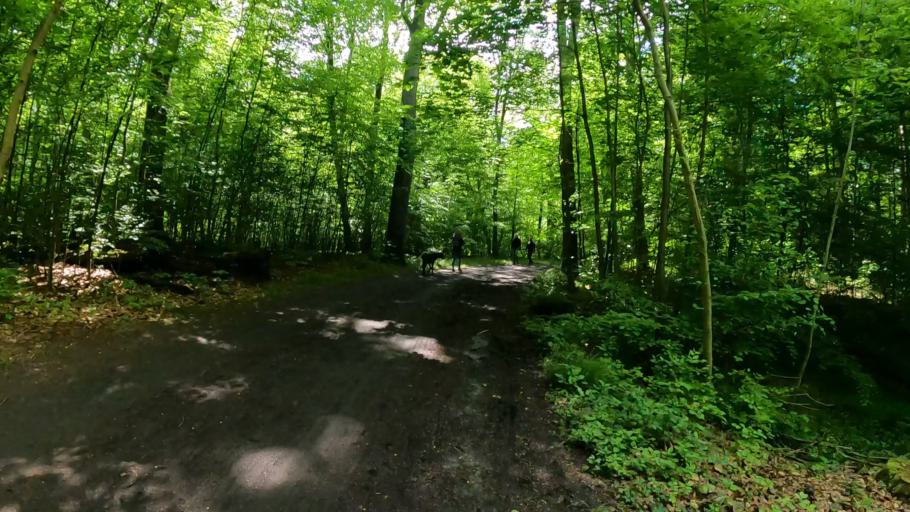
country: DE
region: Hamburg
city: Wohldorf-Ohlstedt
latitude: 53.6875
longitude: 10.1203
